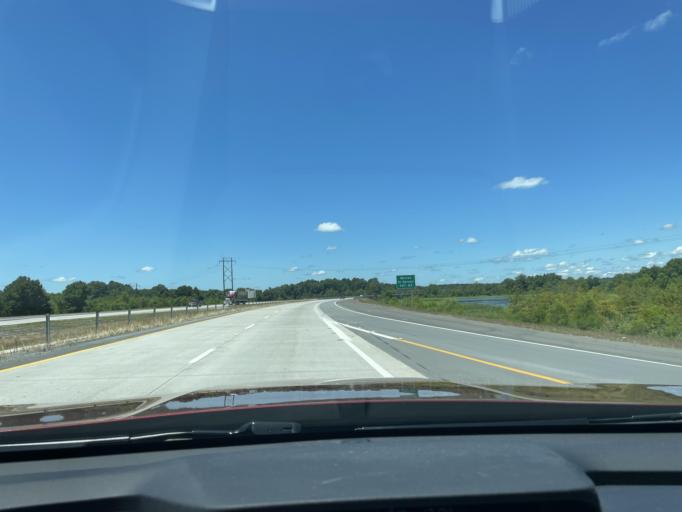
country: US
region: Arkansas
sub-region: Jefferson County
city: Pine Bluff
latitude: 34.1726
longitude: -91.9940
